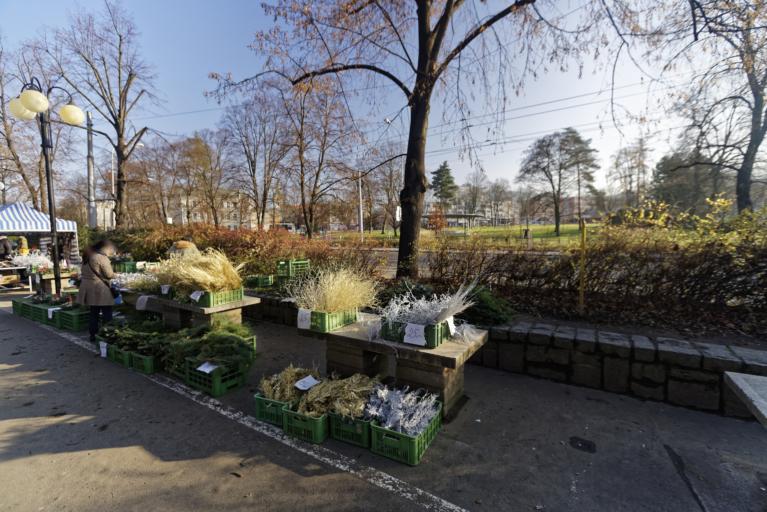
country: CZ
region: Zlin
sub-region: Okres Zlin
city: Zlin
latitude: 49.2251
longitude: 17.6638
